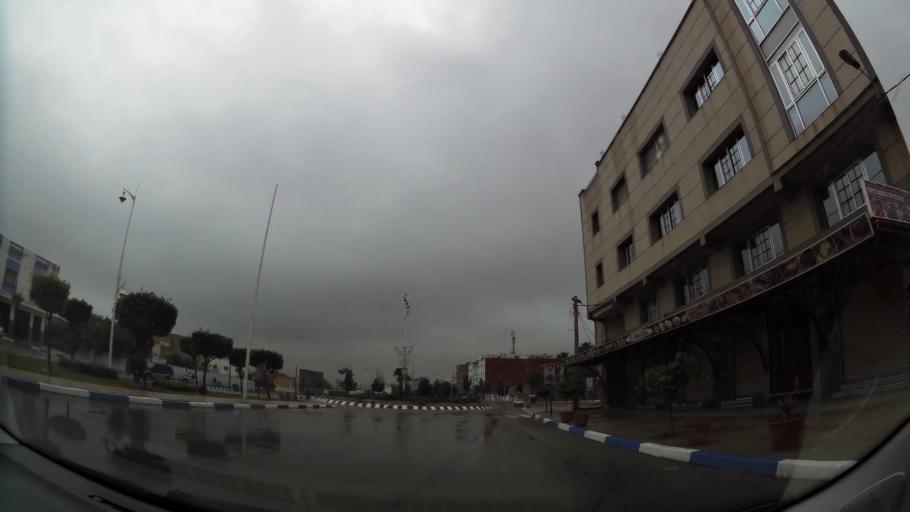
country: MA
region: Oriental
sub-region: Nador
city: Nador
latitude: 35.1664
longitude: -2.9505
